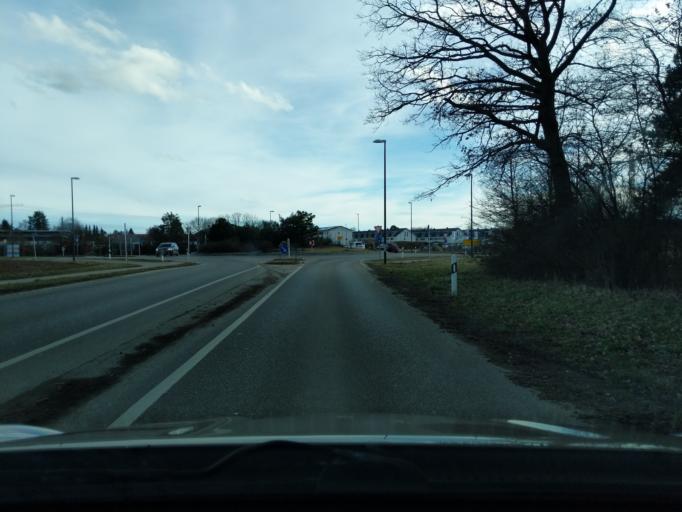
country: DE
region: Bavaria
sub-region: Upper Bavaria
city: Vaterstetten
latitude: 48.1169
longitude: 11.7689
